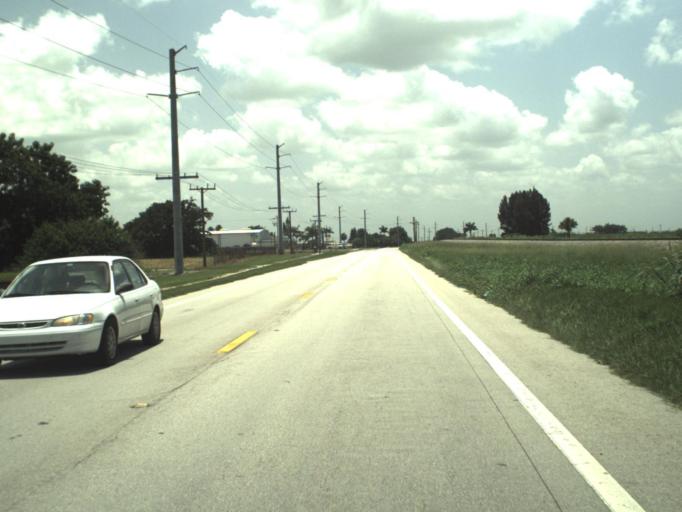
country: US
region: Florida
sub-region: Palm Beach County
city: Pahokee
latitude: 26.8355
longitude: -80.6445
